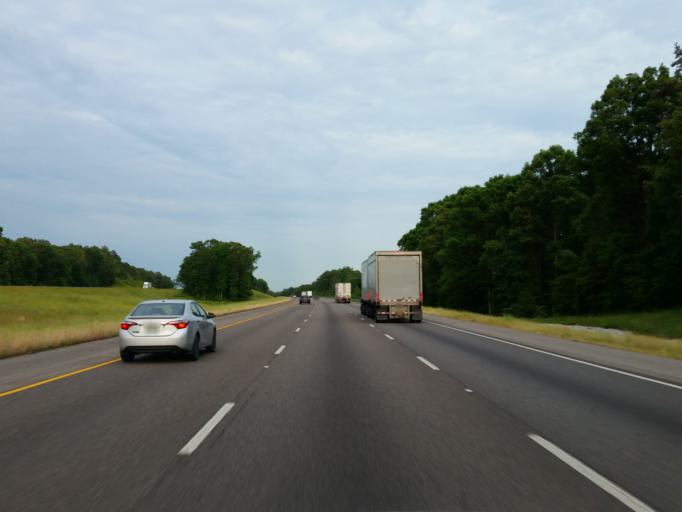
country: US
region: Alabama
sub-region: Calhoun County
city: Bynum
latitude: 33.5770
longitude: -86.0036
